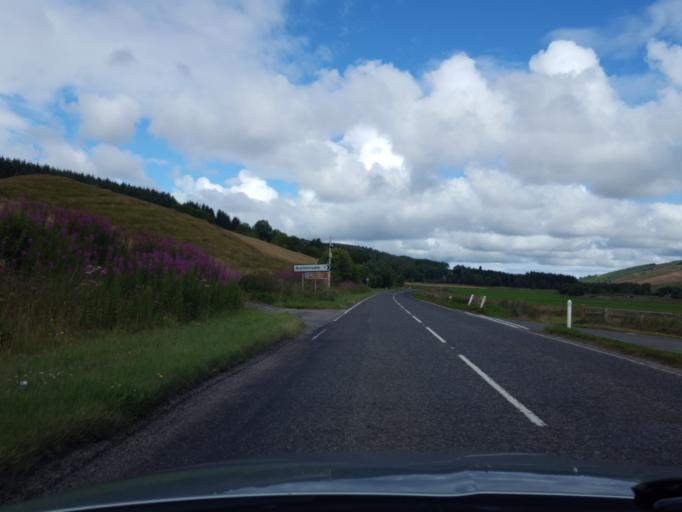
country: GB
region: Scotland
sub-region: Moray
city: Rothes
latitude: 57.5471
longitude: -3.2354
